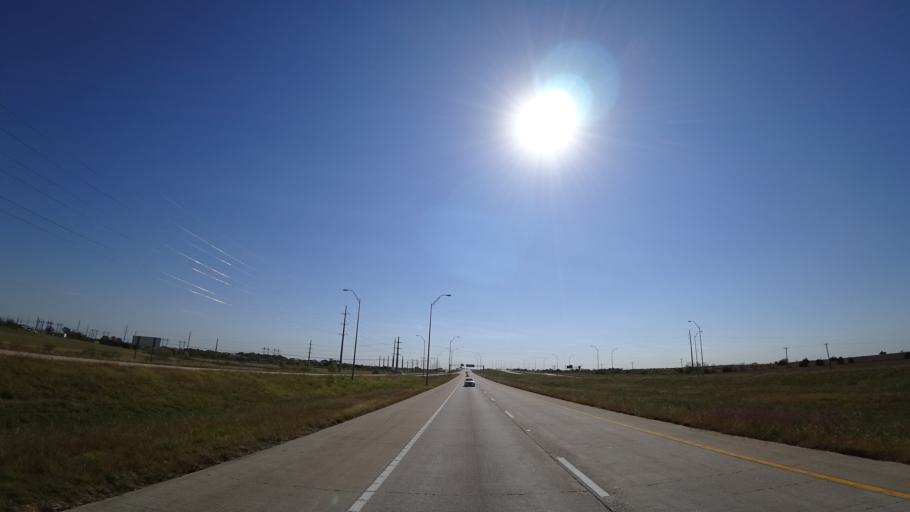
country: US
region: Texas
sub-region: Travis County
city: Pflugerville
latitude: 30.4126
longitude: -97.5848
